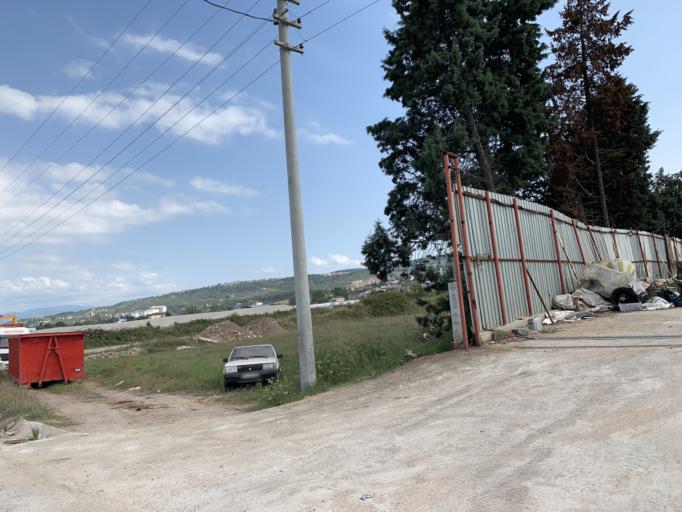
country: TR
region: Yalova
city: Taskopru
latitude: 40.6925
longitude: 29.4478
